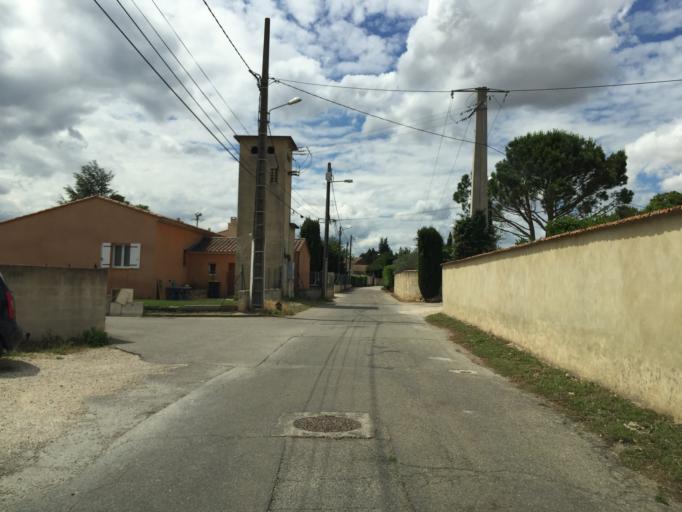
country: FR
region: Provence-Alpes-Cote d'Azur
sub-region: Departement du Vaucluse
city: Sorgues
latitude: 44.0162
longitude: 4.8672
